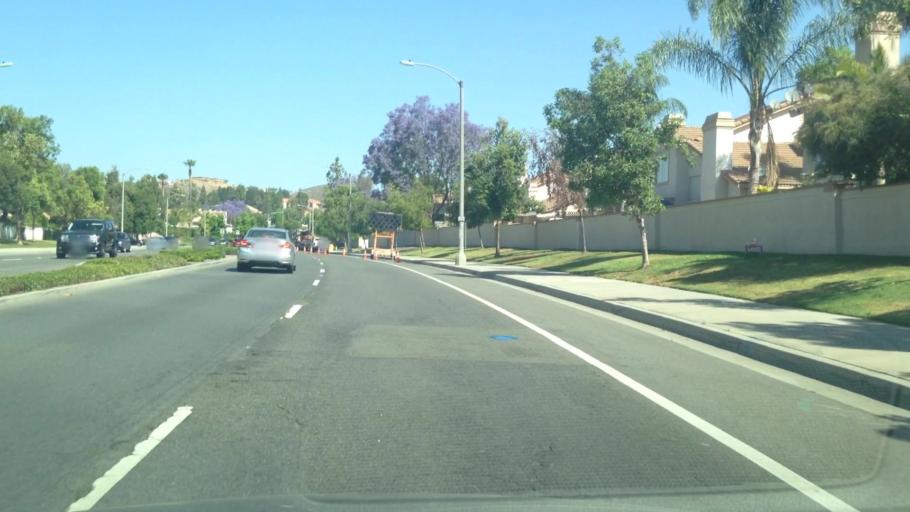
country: US
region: California
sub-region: Riverside County
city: Home Gardens
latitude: 33.8953
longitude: -117.5254
